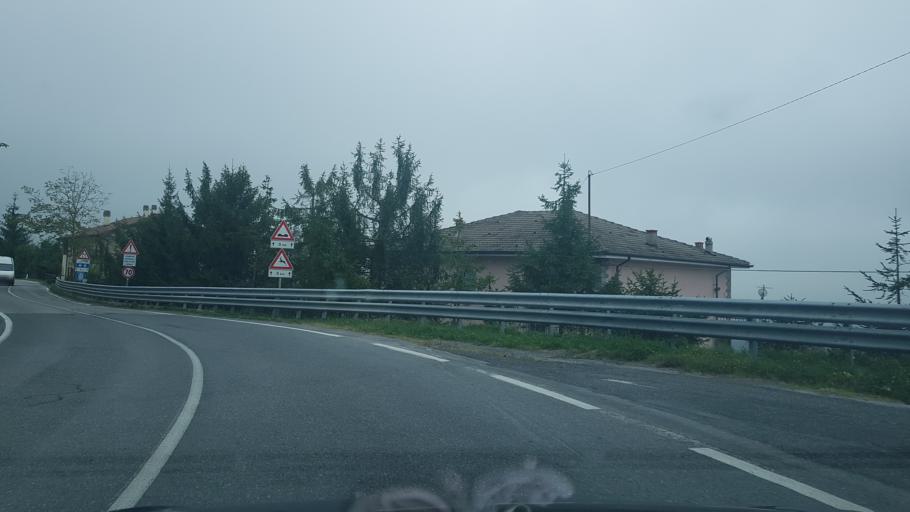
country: IT
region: Piedmont
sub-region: Provincia di Cuneo
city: Sale San Giovanni
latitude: 44.4171
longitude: 8.0883
